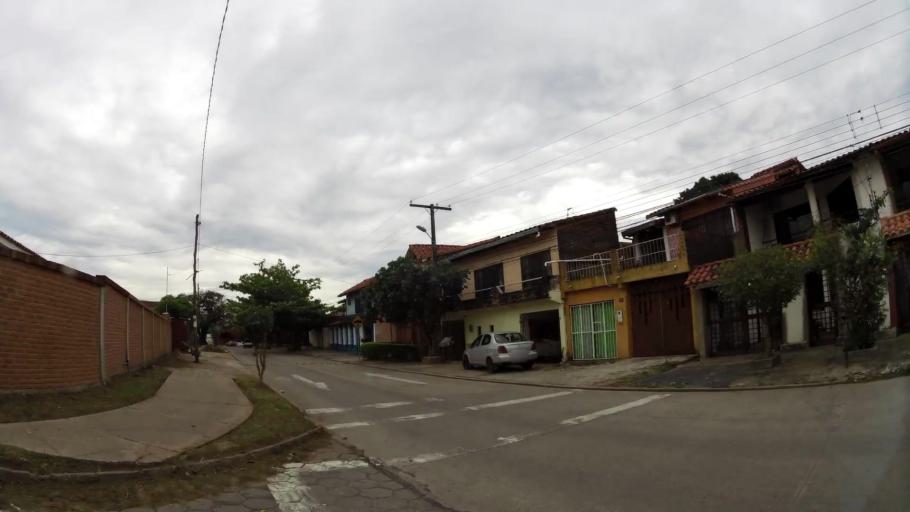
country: BO
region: Santa Cruz
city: Santa Cruz de la Sierra
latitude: -17.7733
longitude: -63.1604
